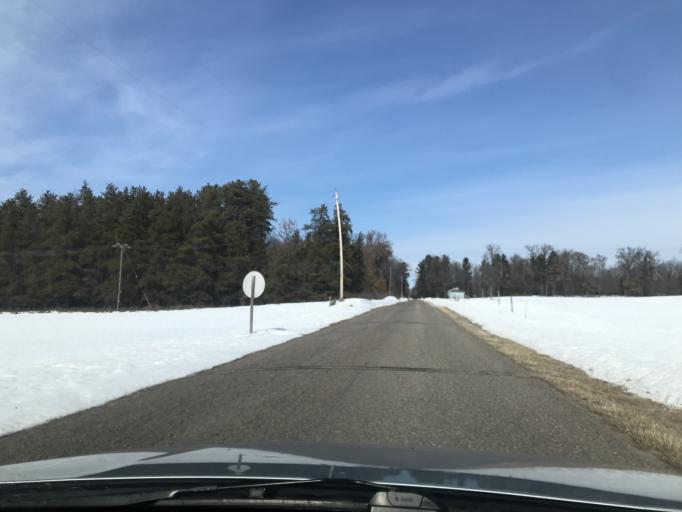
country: US
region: Wisconsin
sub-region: Marinette County
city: Peshtigo
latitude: 45.2200
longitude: -87.9630
